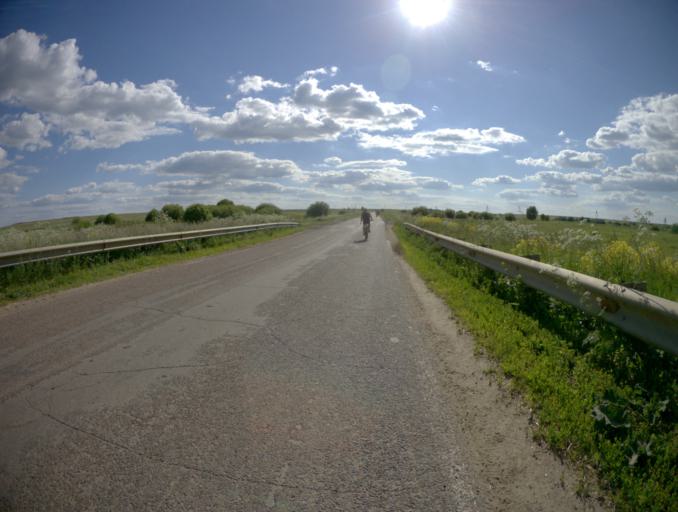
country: RU
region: Vladimir
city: Suzdal'
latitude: 56.3421
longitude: 40.3264
